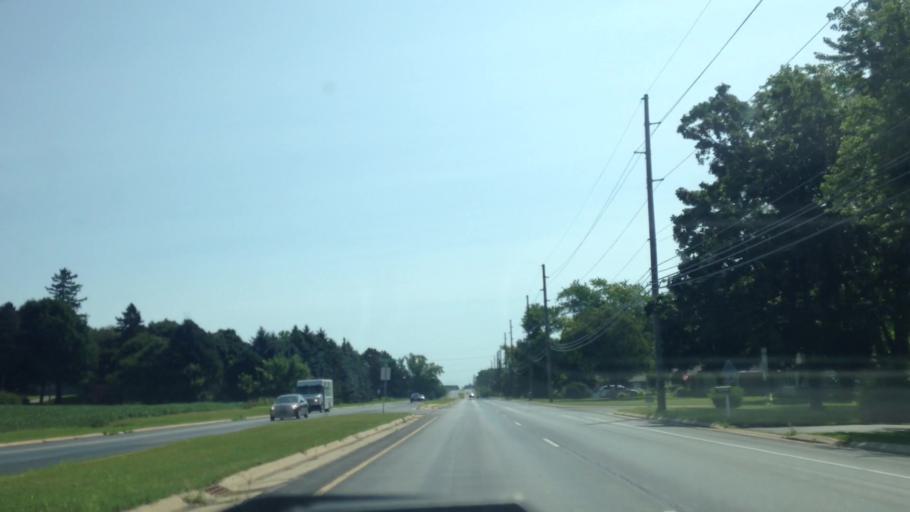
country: US
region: Wisconsin
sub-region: Waukesha County
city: Menomonee Falls
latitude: 43.1922
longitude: -88.1589
